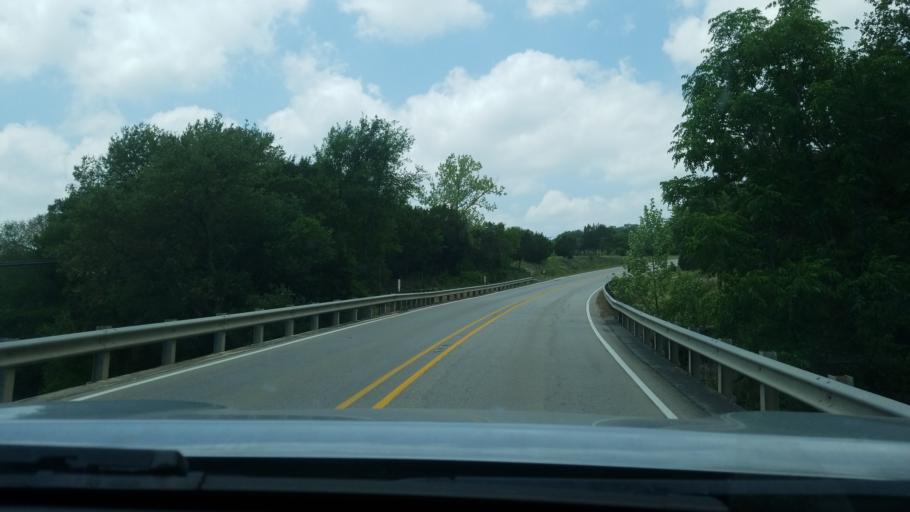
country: US
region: Texas
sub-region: Hays County
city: Dripping Springs
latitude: 30.1436
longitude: -98.0488
